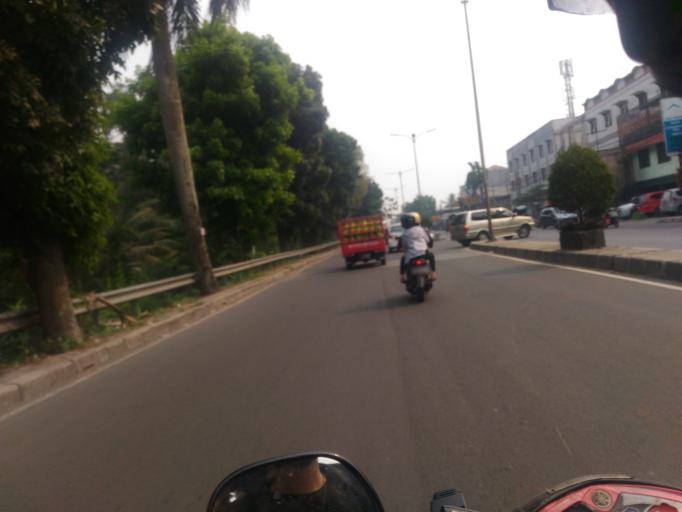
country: ID
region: West Java
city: Cibinong
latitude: -6.4943
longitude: 106.8451
